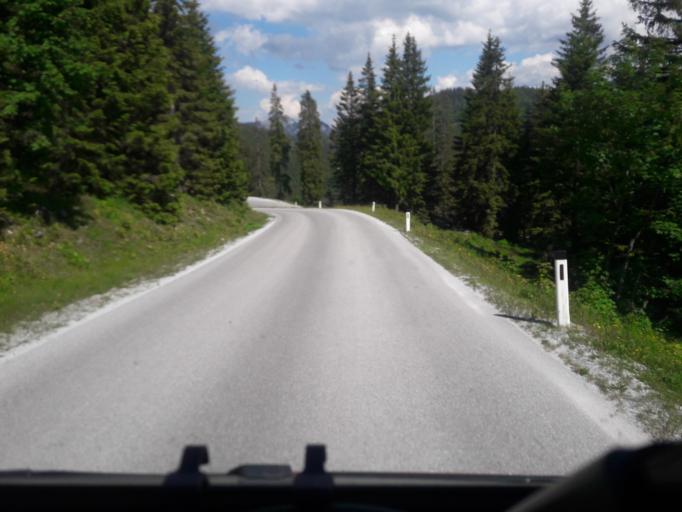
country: AT
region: Styria
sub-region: Politischer Bezirk Liezen
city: Tauplitz
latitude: 47.5852
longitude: 13.9661
